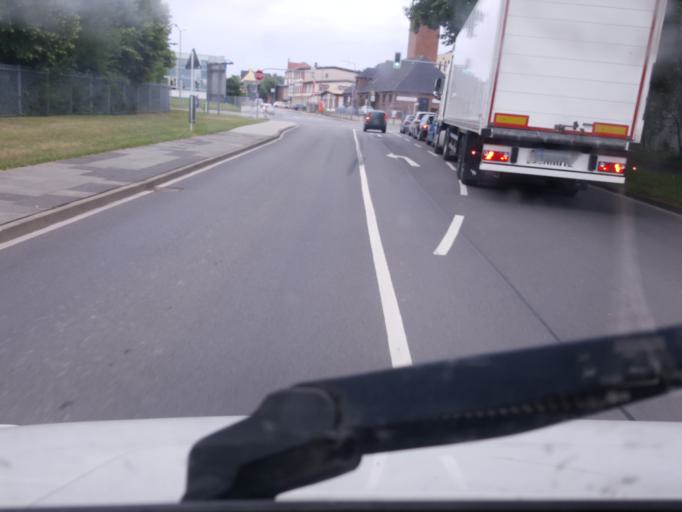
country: DE
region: North Rhine-Westphalia
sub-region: Regierungsbezirk Detmold
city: Minden
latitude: 52.2981
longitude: 8.9030
